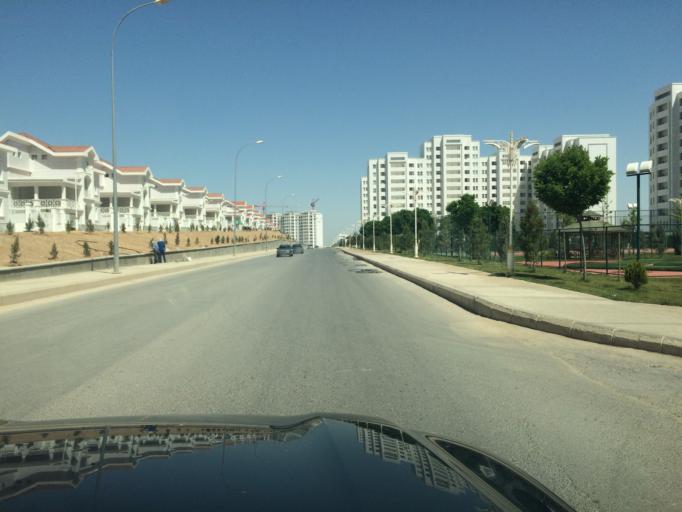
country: TM
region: Ahal
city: Ashgabat
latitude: 37.9319
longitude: 58.3655
